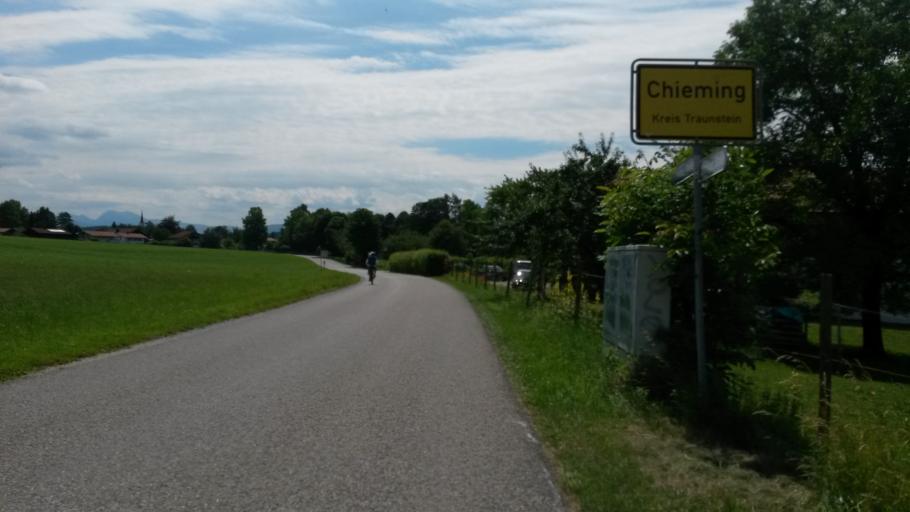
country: DE
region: Bavaria
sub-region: Upper Bavaria
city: Chieming
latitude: 47.8979
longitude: 12.5305
